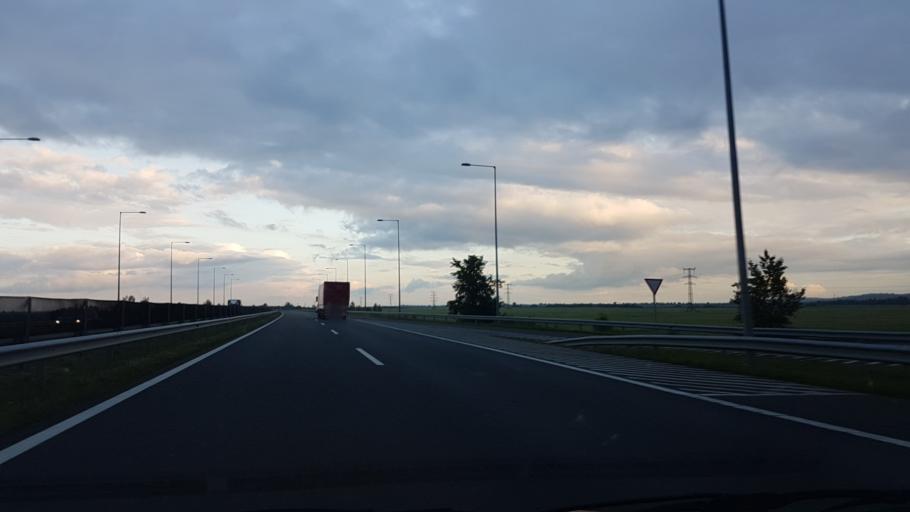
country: HU
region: Borsod-Abauj-Zemplen
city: Malyi
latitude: 48.0368
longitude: 20.8578
